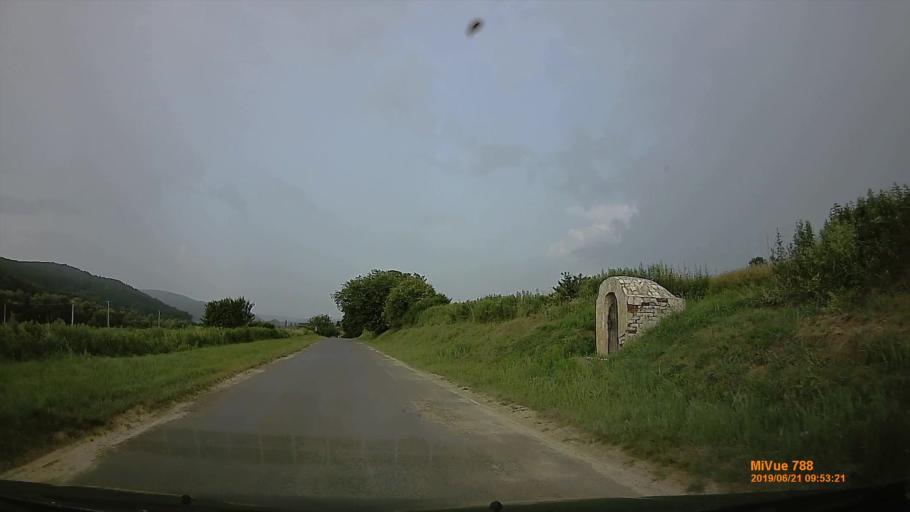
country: HU
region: Baranya
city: Sasd
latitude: 46.2370
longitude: 18.0082
